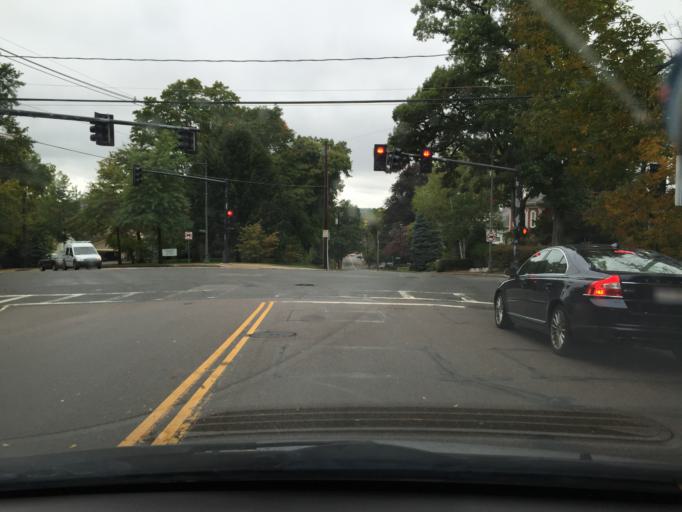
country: US
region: Massachusetts
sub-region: Middlesex County
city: Winchester
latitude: 42.4527
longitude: -71.1290
